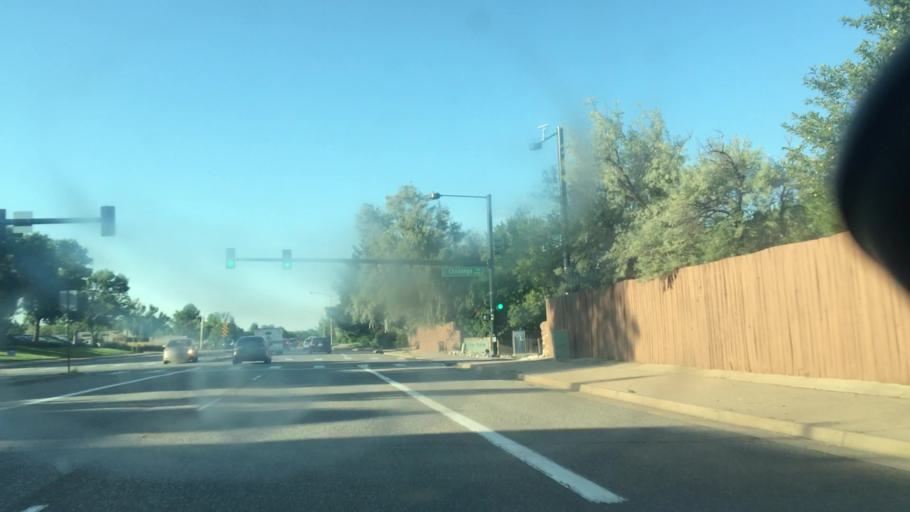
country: US
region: Colorado
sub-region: Arapahoe County
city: Castlewood
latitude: 39.6275
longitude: -104.8854
